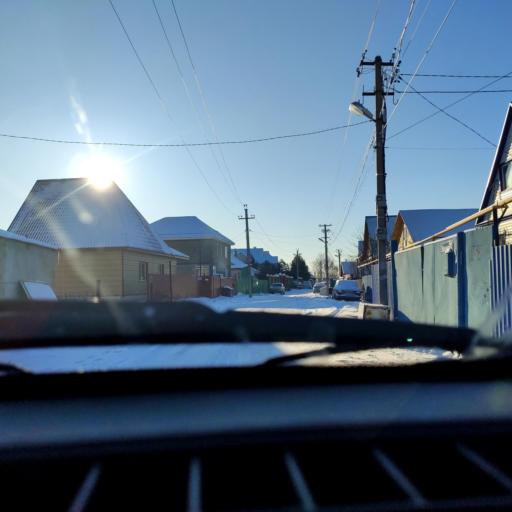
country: RU
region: Bashkortostan
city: Ufa
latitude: 54.6938
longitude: 55.9529
